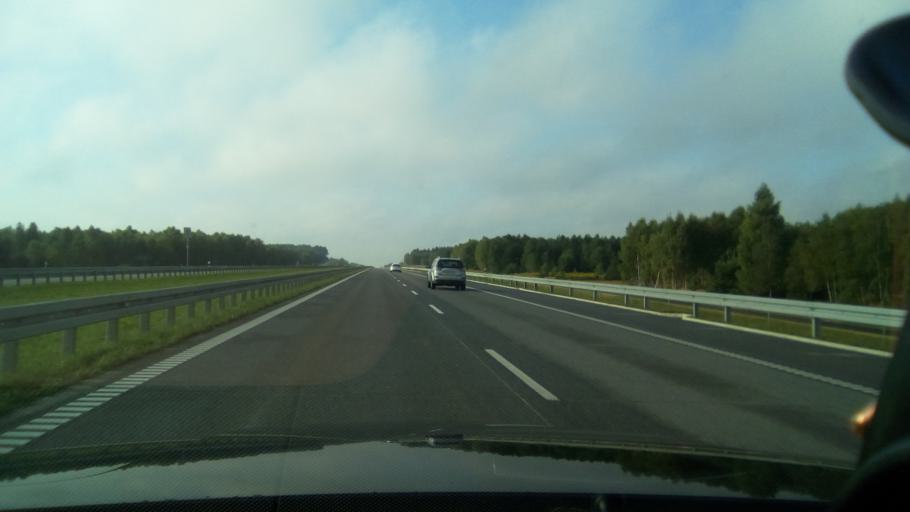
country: PL
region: Silesian Voivodeship
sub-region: Powiat czestochowski
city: Konopiska
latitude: 50.7208
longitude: 19.0573
